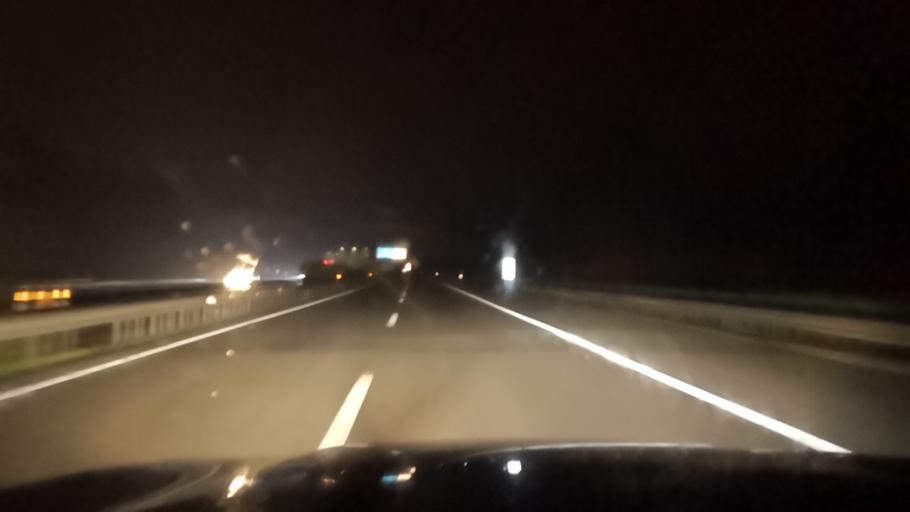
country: PT
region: Leiria
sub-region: Pombal
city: Pombal
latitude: 39.9438
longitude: -8.6753
